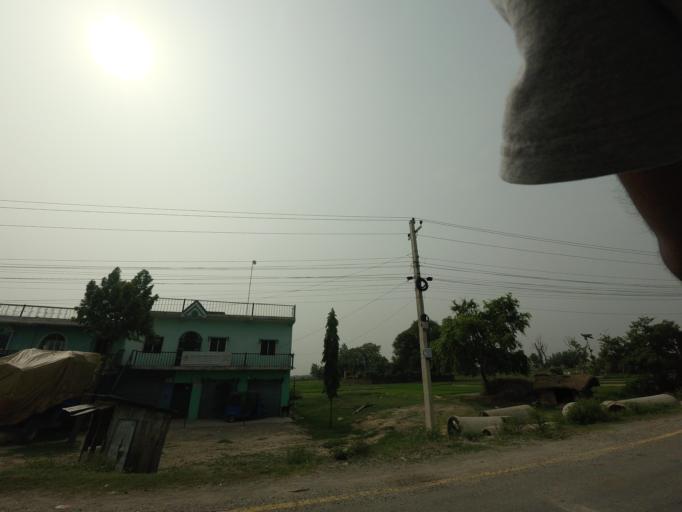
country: NP
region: Western Region
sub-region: Lumbini Zone
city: Bhairahawa
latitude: 27.5123
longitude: 83.3905
